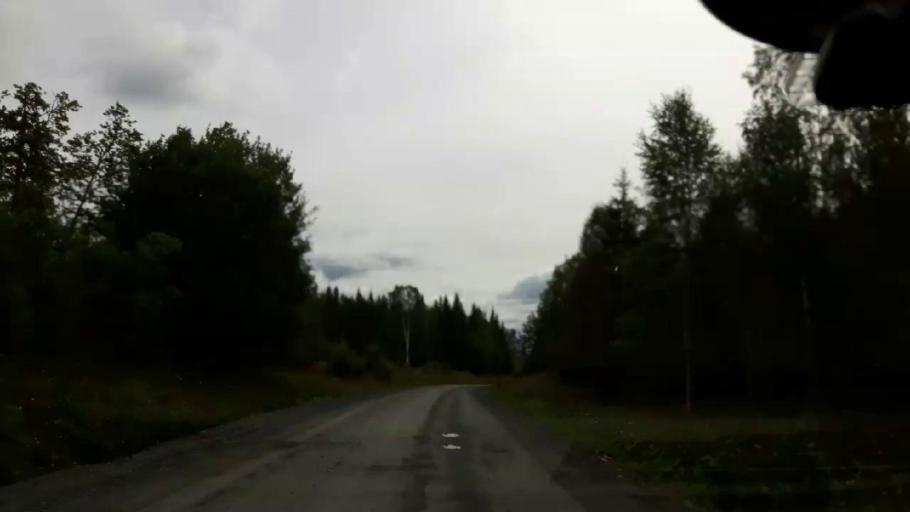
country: SE
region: Jaemtland
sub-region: Krokoms Kommun
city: Valla
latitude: 63.6508
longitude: 13.9852
